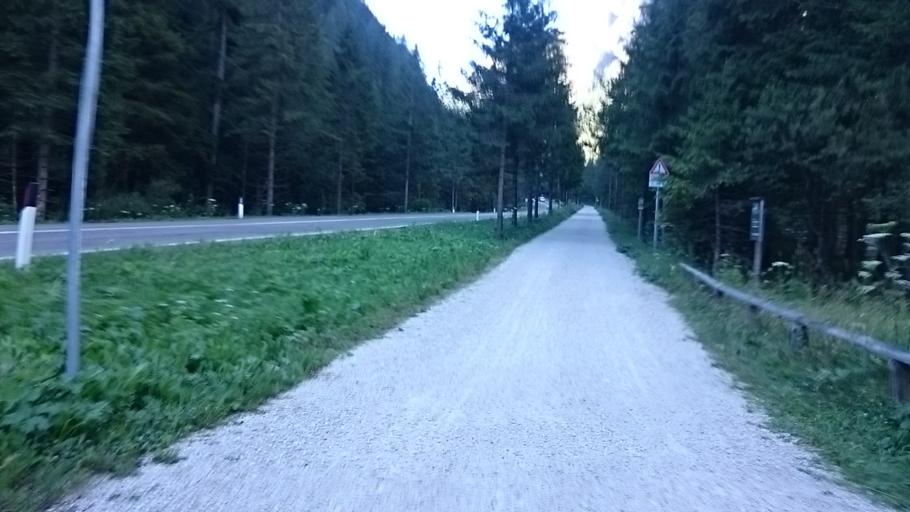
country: IT
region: Trentino-Alto Adige
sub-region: Bolzano
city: Dobbiaco
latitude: 46.6763
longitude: 12.2222
